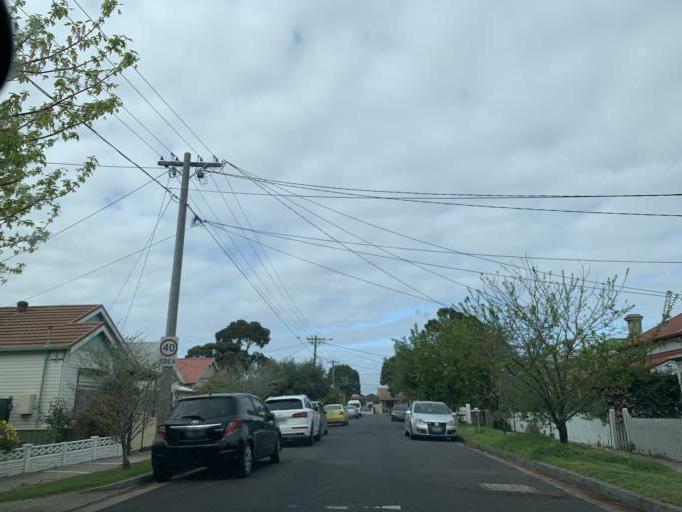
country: AU
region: Victoria
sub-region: Moreland
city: Coburg North
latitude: -37.7379
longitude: 144.9602
